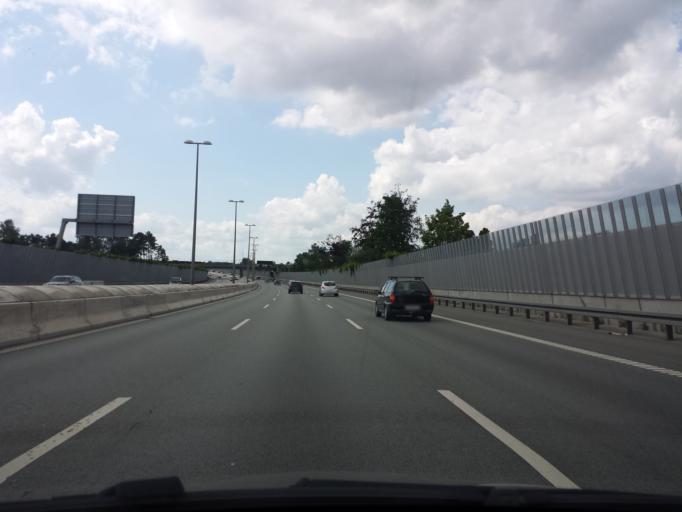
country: DK
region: Capital Region
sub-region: Gladsaxe Municipality
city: Buddinge
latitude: 55.7476
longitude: 12.4662
